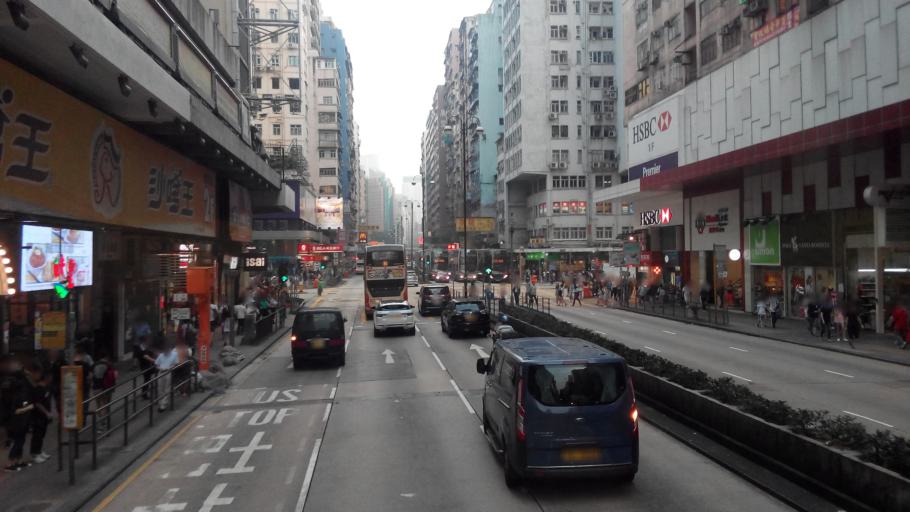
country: HK
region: Kowloon City
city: Kowloon
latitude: 22.3136
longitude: 114.1705
